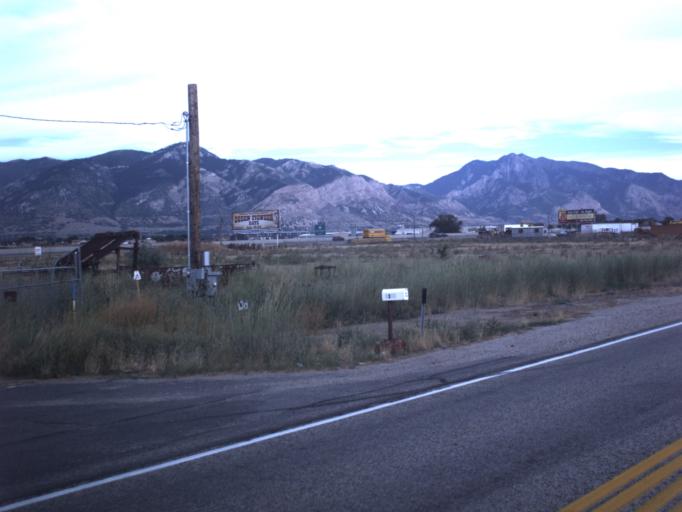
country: US
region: Utah
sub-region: Weber County
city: Farr West
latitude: 41.3197
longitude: -112.0293
